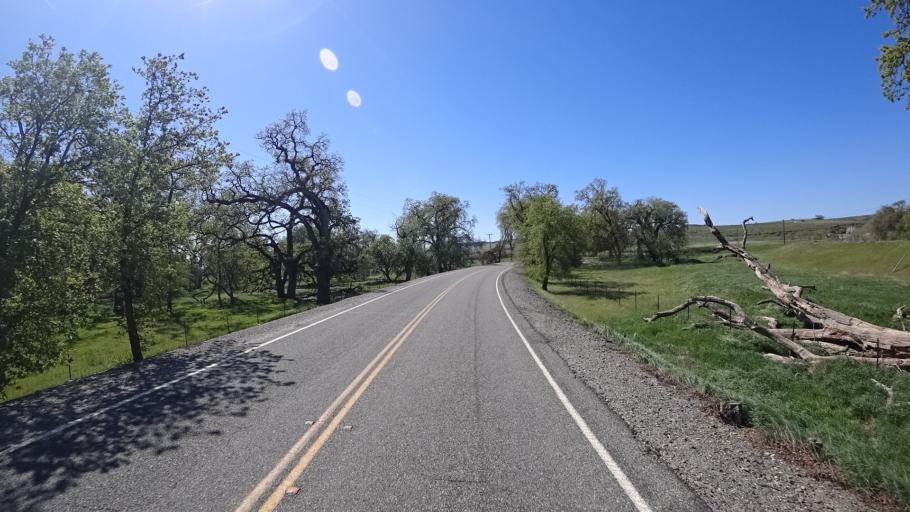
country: US
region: California
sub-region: Glenn County
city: Orland
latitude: 39.8164
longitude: -122.3255
